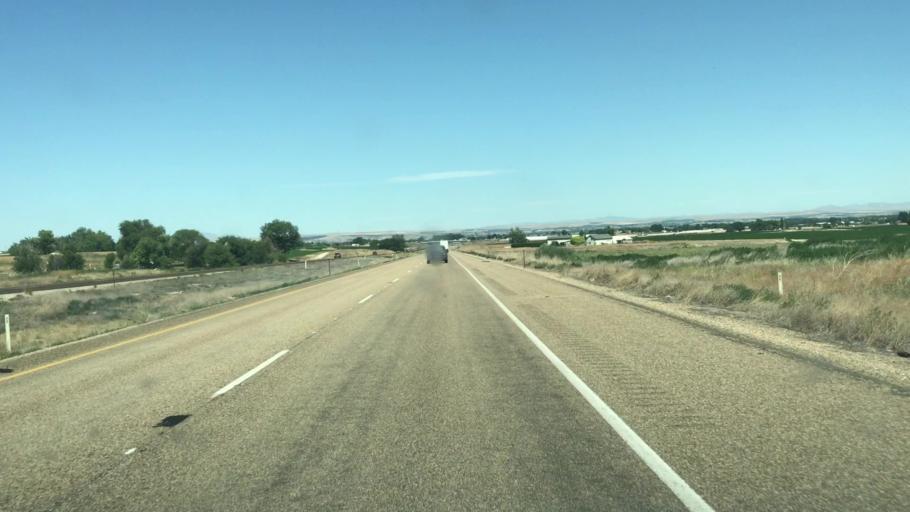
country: US
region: Idaho
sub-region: Payette County
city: New Plymouth
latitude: 43.9480
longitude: -116.8798
